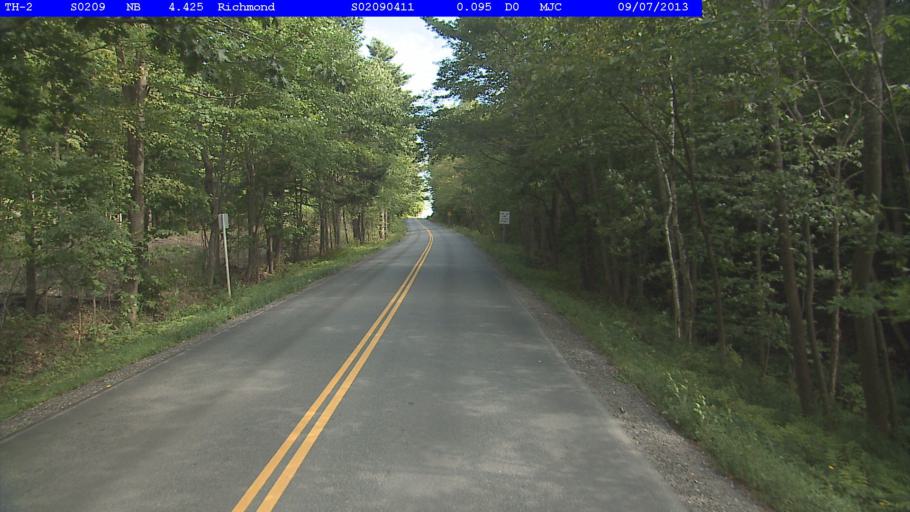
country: US
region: Vermont
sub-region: Chittenden County
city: Hinesburg
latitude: 44.3728
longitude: -73.0642
